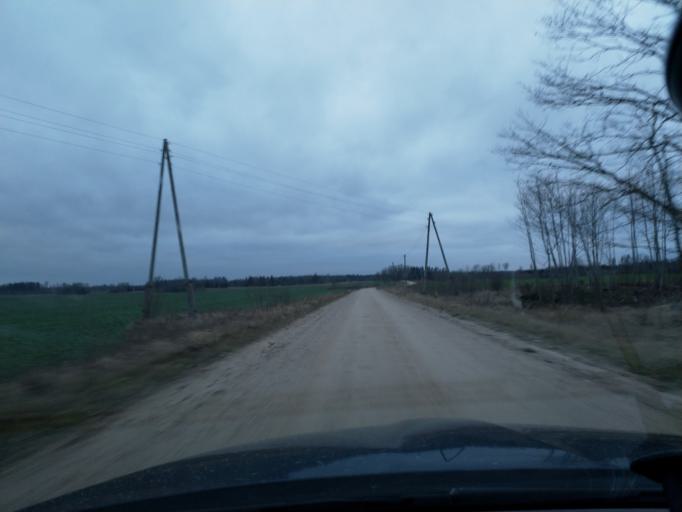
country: LV
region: Saldus Rajons
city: Saldus
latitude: 56.8961
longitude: 22.3187
